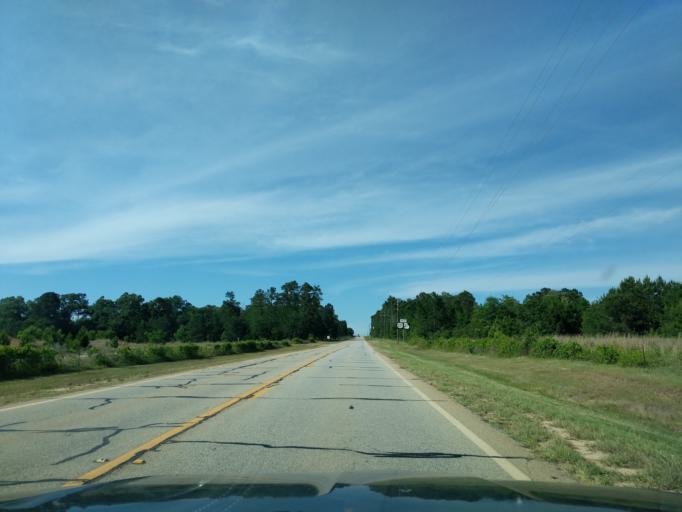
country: US
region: Georgia
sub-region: Jefferson County
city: Wrens
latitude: 33.2799
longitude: -82.3854
